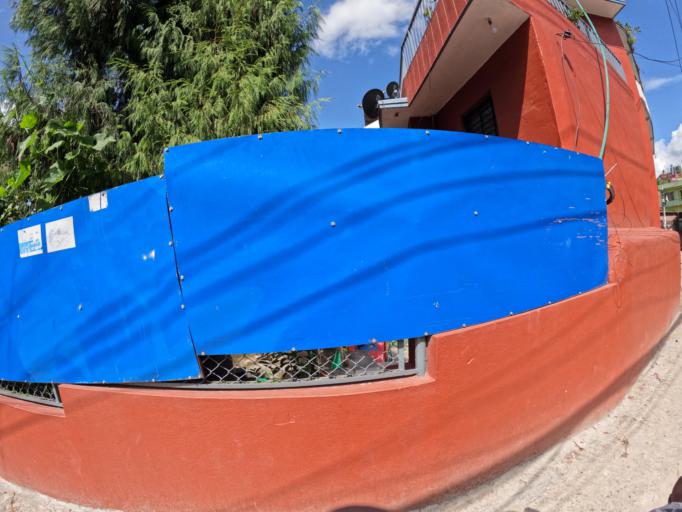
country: NP
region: Central Region
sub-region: Bagmati Zone
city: Kathmandu
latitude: 27.7438
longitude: 85.3322
